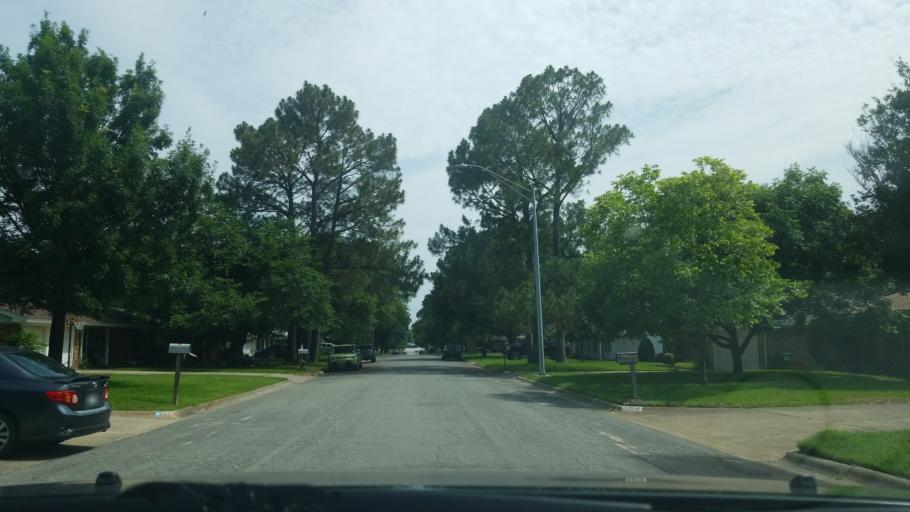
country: US
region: Texas
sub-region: Denton County
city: Denton
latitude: 33.2348
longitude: -97.1514
